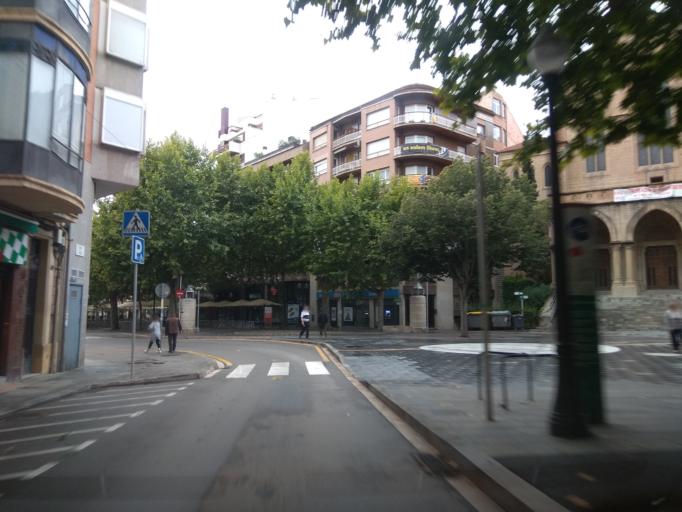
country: ES
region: Catalonia
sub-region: Provincia de Barcelona
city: Manresa
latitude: 41.7286
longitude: 1.8240
